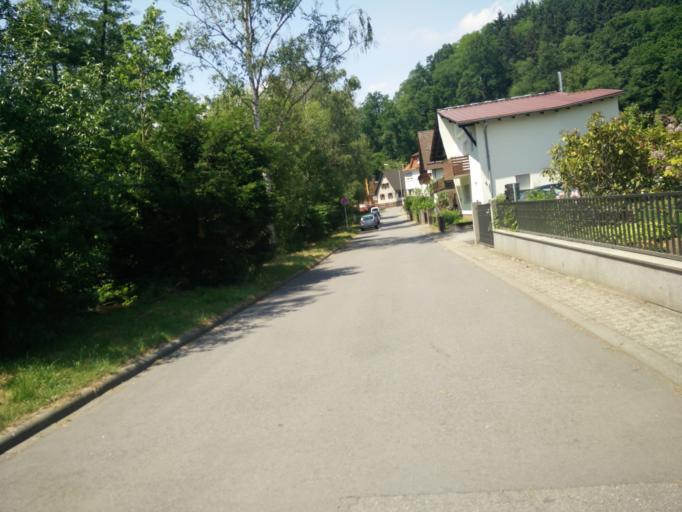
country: DE
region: Hesse
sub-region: Regierungsbezirk Darmstadt
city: Birkenau
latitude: 49.5612
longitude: 8.6982
